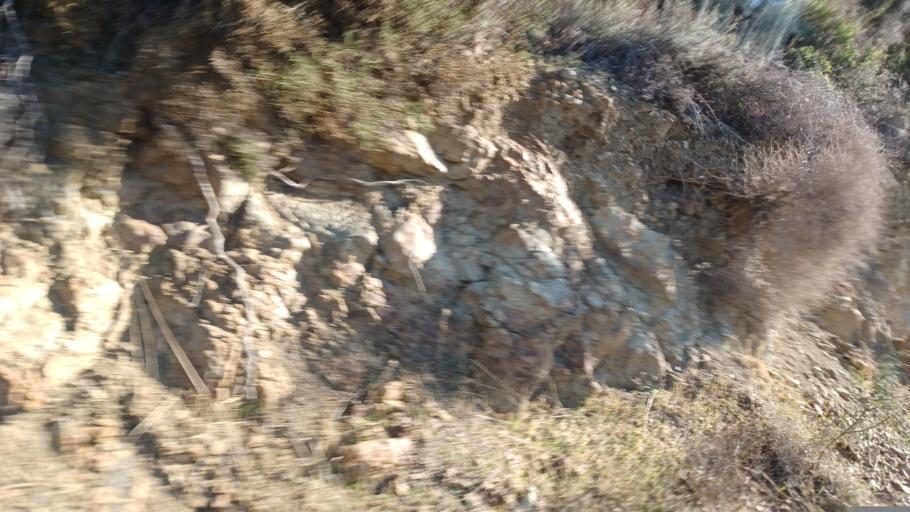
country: CY
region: Pafos
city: Polis
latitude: 35.0140
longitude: 32.4946
